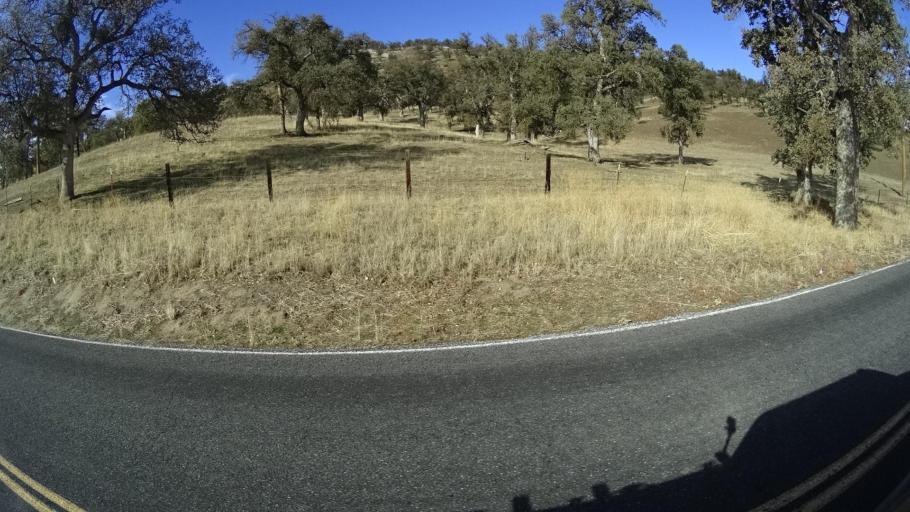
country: US
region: California
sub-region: Kern County
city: Alta Sierra
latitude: 35.6720
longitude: -118.7409
